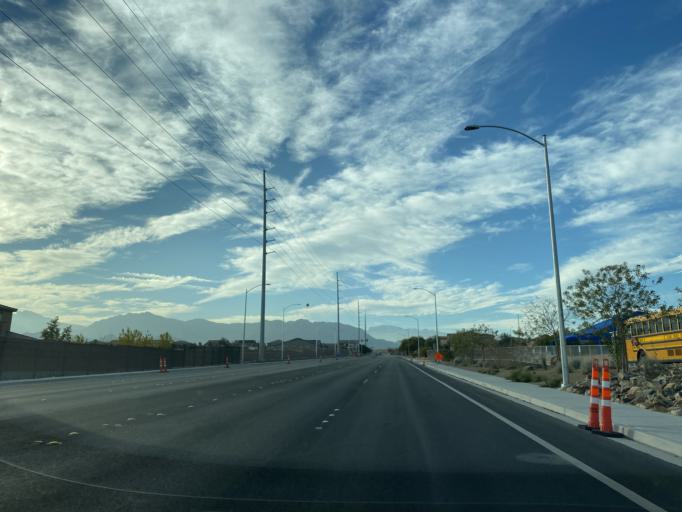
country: US
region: Nevada
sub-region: Clark County
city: Summerlin South
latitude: 36.2994
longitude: -115.3097
